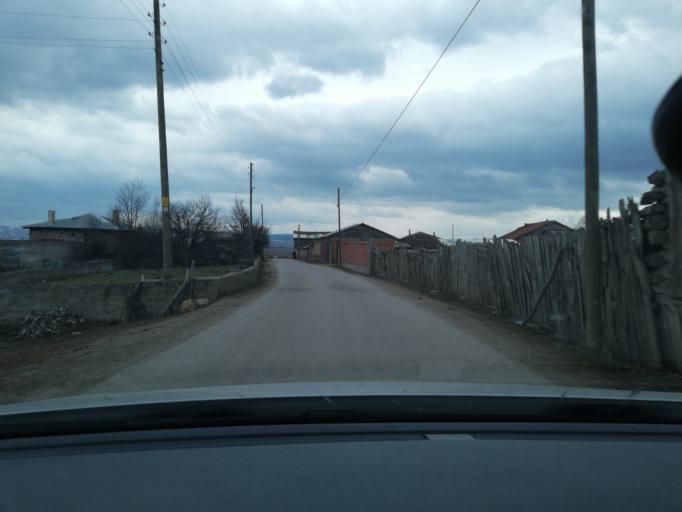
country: TR
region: Bolu
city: Gerede
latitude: 40.7326
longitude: 32.2154
